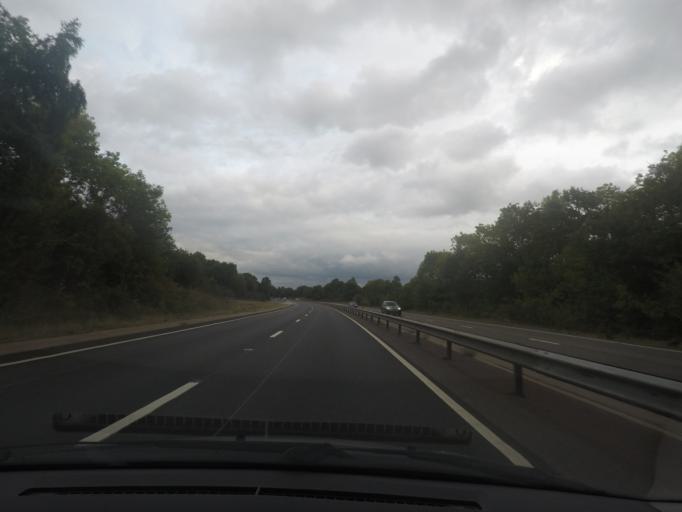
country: GB
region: England
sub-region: Oxfordshire
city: Radley
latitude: 51.6989
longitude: -1.2660
